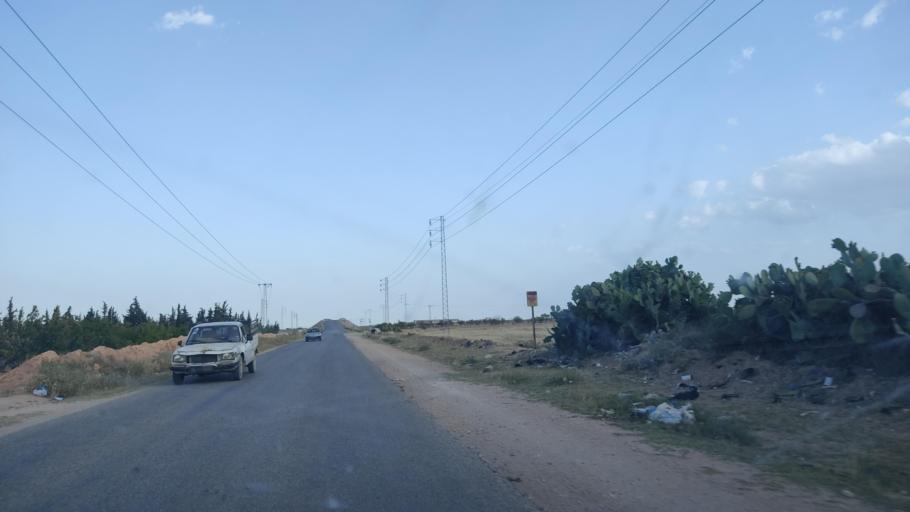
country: TN
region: Safaqis
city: Sfax
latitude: 34.8289
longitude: 10.6395
